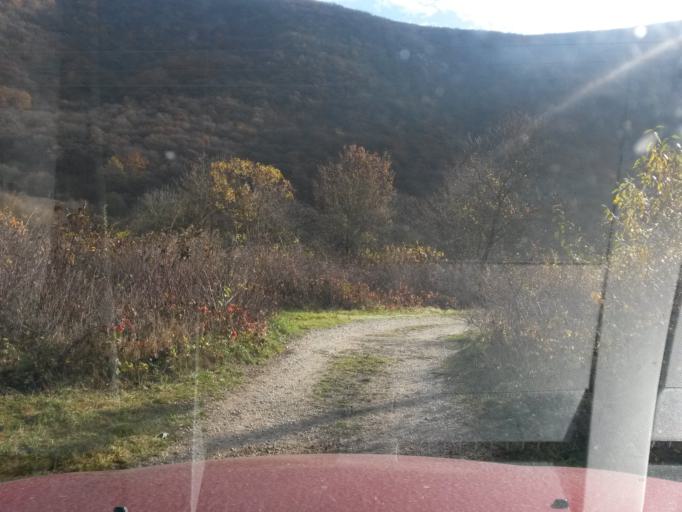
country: SK
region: Kosicky
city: Roznava
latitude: 48.5890
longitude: 20.4803
